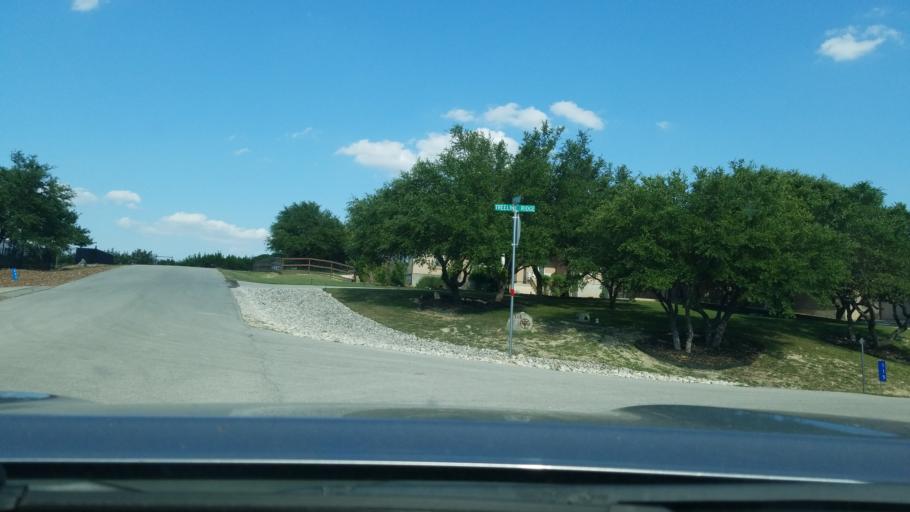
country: US
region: Texas
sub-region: Comal County
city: Bulverde
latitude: 29.8214
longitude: -98.3976
